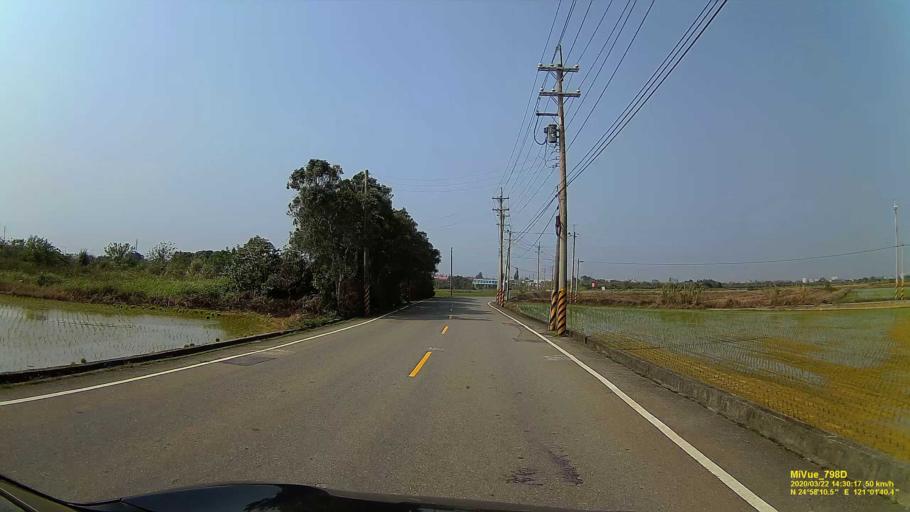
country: TW
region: Taiwan
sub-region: Hsinchu
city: Zhubei
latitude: 24.9697
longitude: 121.0281
